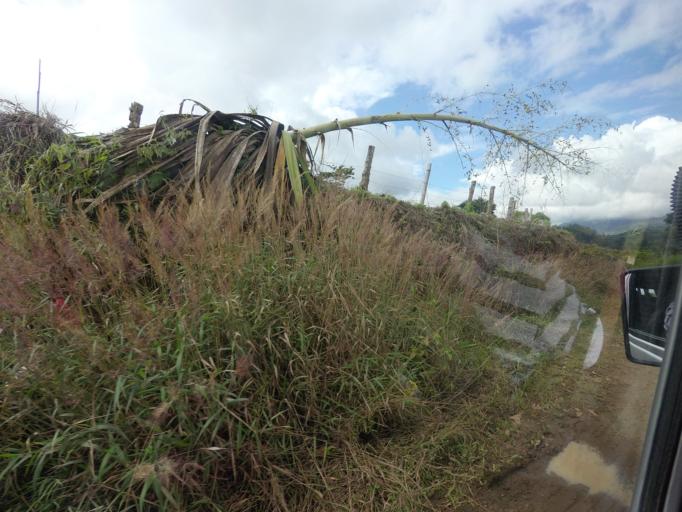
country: CO
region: Huila
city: San Agustin
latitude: 1.9236
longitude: -76.2931
